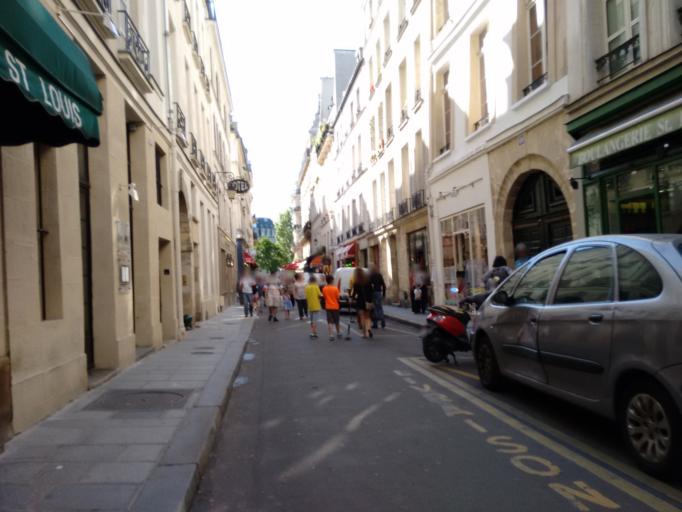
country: FR
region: Ile-de-France
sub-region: Paris
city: Paris
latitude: 48.8526
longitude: 2.3546
